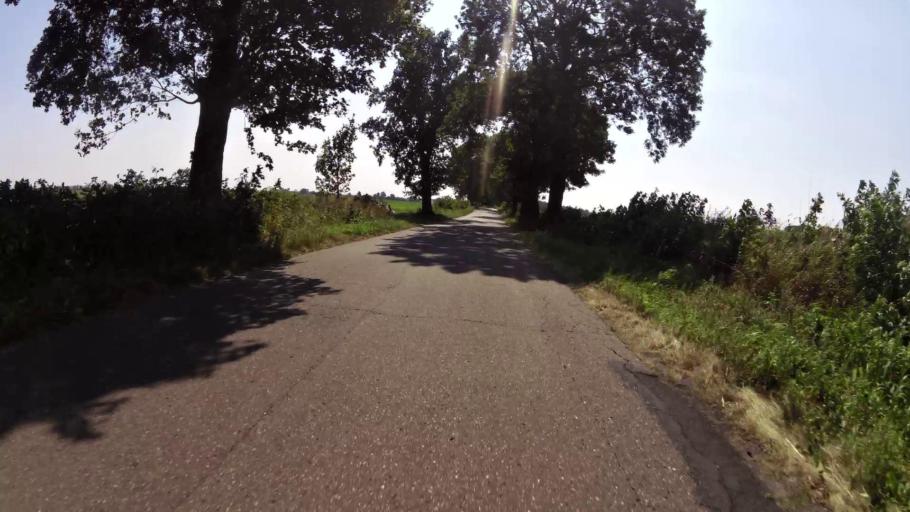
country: PL
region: West Pomeranian Voivodeship
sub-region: Powiat walecki
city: Walcz
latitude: 53.2210
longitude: 16.5007
